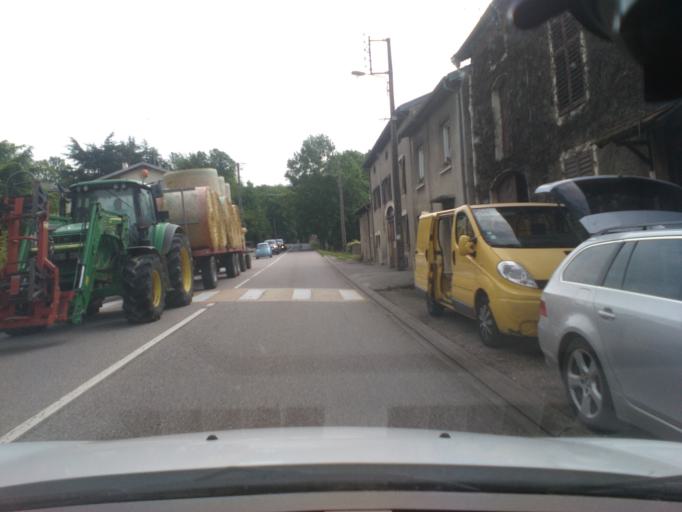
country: FR
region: Lorraine
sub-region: Departement de Meurthe-et-Moselle
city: Pulligny
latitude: 48.5245
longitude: 6.1660
